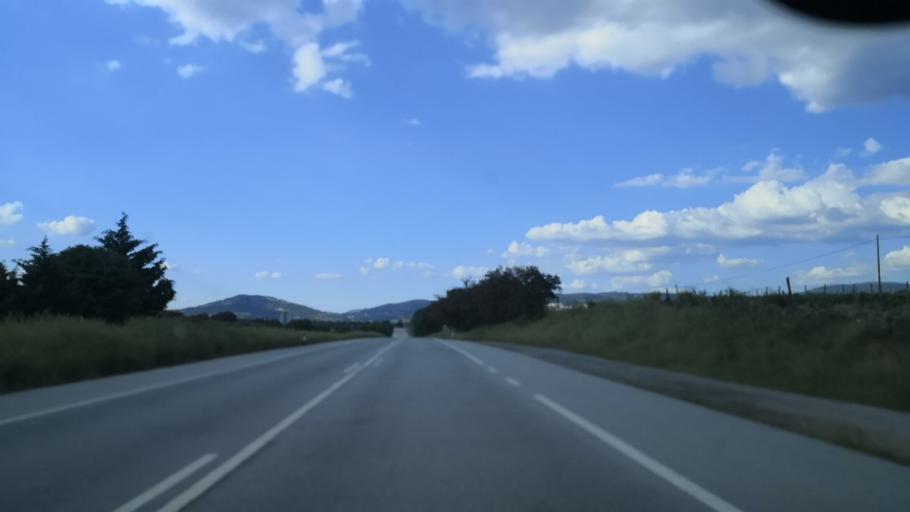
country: PT
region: Portalegre
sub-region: Portalegre
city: Portalegre
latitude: 39.2447
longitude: -7.4500
